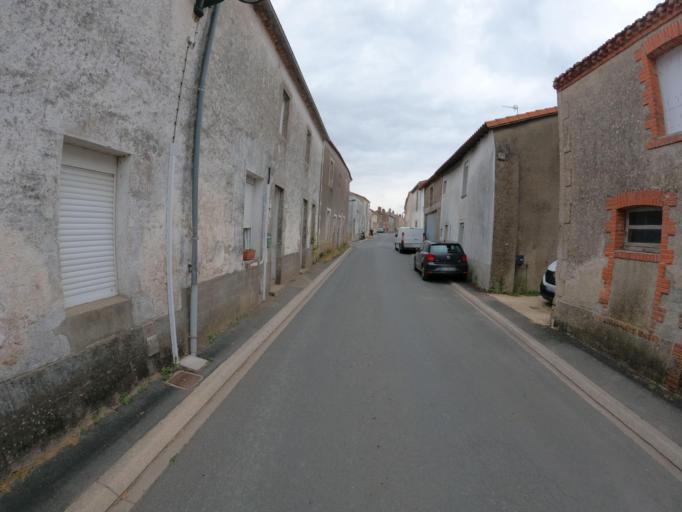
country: FR
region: Pays de la Loire
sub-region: Departement de la Vendee
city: La Boissiere-de-Montaigu
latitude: 46.9800
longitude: -1.1743
